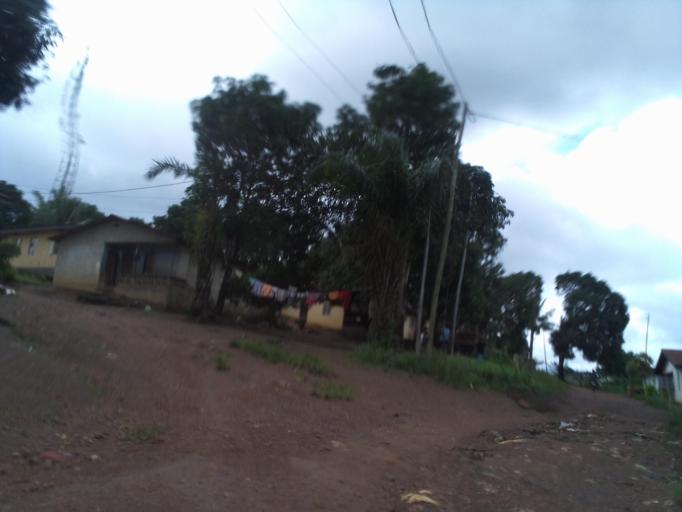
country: SL
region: Eastern Province
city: Kenema
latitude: 7.8591
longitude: -11.1884
